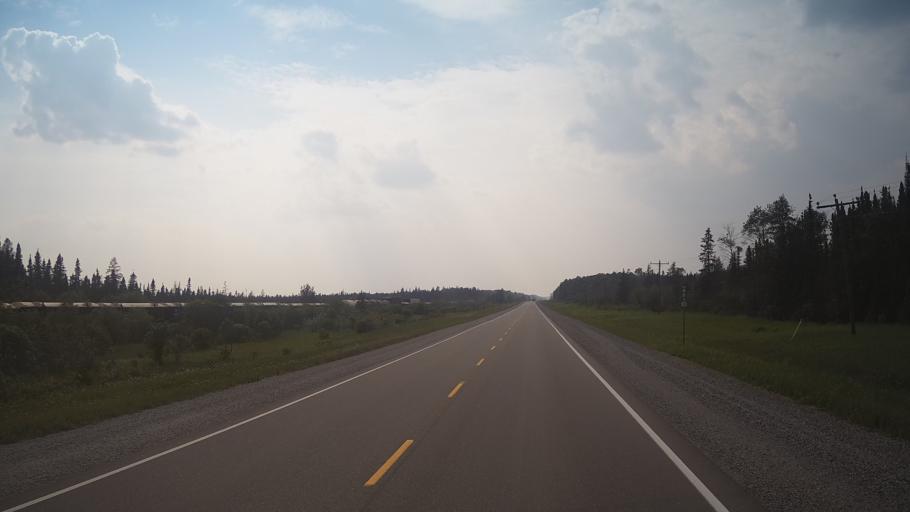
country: CA
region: Ontario
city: Kapuskasing
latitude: 49.5603
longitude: -83.0322
